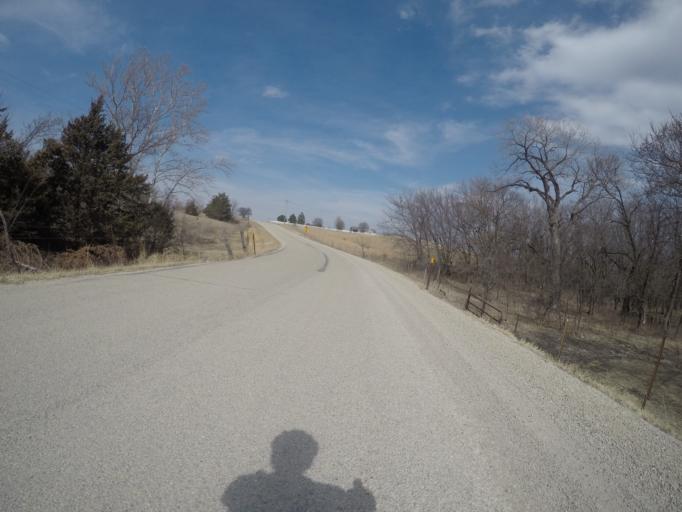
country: US
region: Kansas
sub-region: Geary County
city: Grandview Plaza
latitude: 39.0125
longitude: -96.7455
